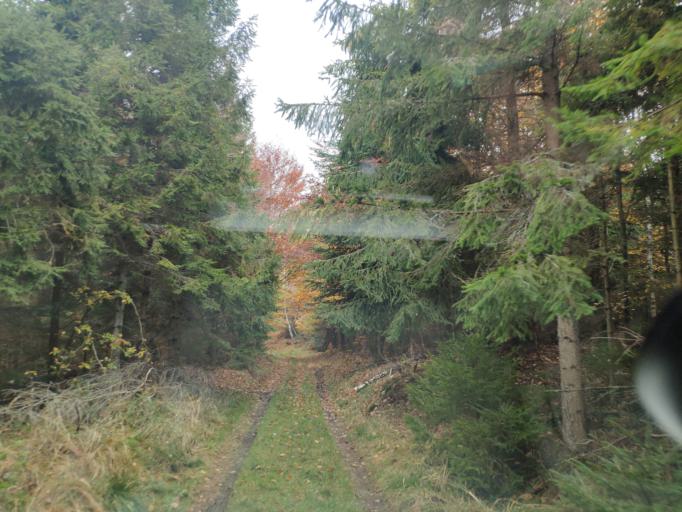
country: SK
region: Kosicky
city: Medzev
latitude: 48.7457
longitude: 20.9876
